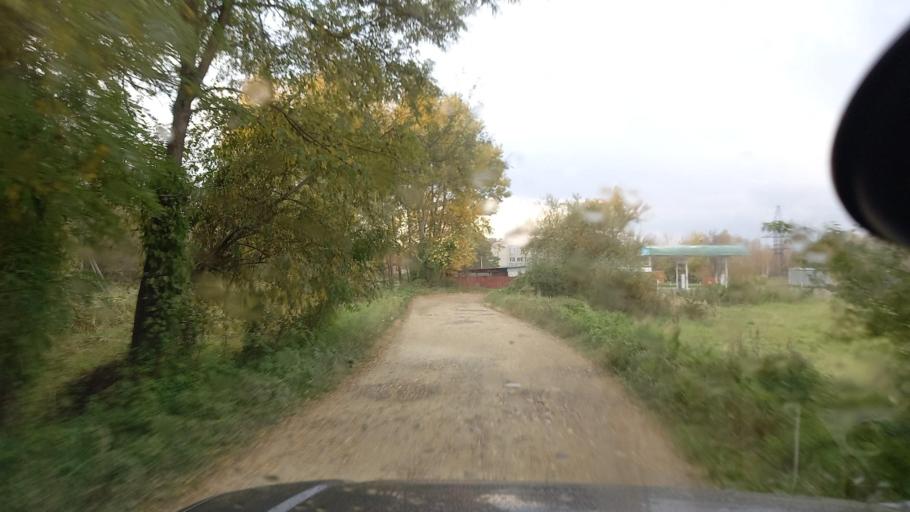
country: RU
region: Krasnodarskiy
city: Shedok
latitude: 44.1732
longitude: 40.8424
